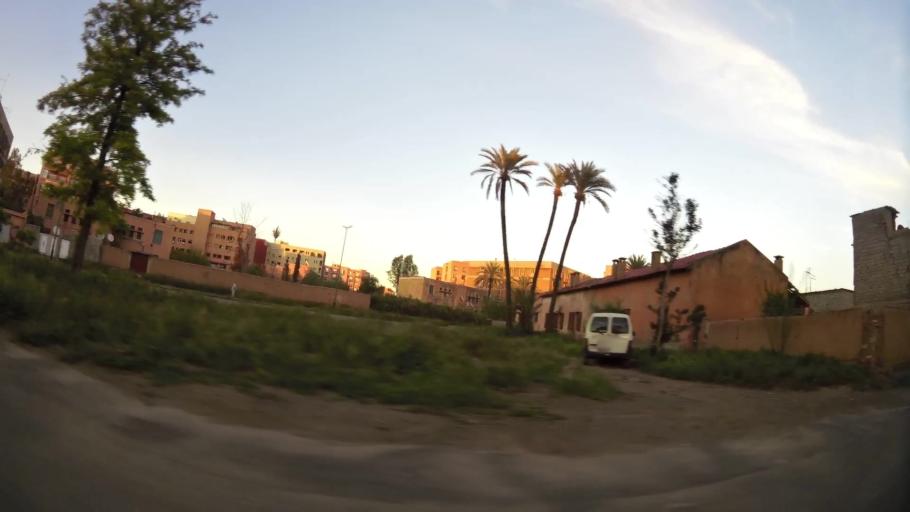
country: MA
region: Marrakech-Tensift-Al Haouz
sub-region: Marrakech
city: Marrakesh
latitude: 31.6380
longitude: -8.0241
